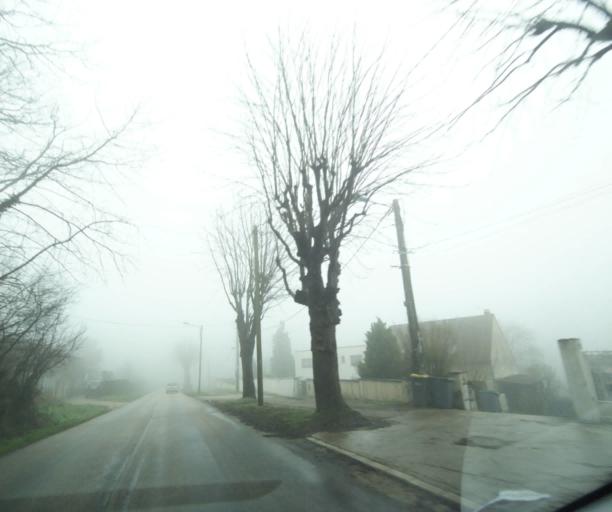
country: FR
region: Ile-de-France
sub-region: Departement de Seine-et-Marne
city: Dammartin-en-Goele
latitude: 49.0500
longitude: 2.6904
